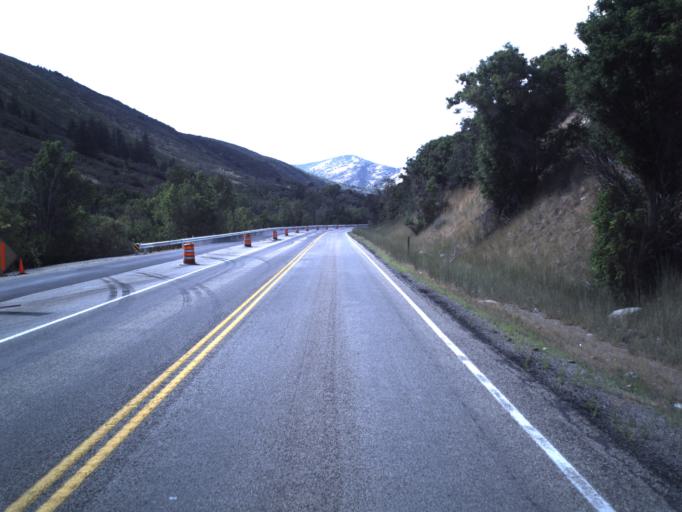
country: US
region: Utah
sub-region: Wasatch County
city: Heber
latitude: 40.4138
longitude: -111.3286
